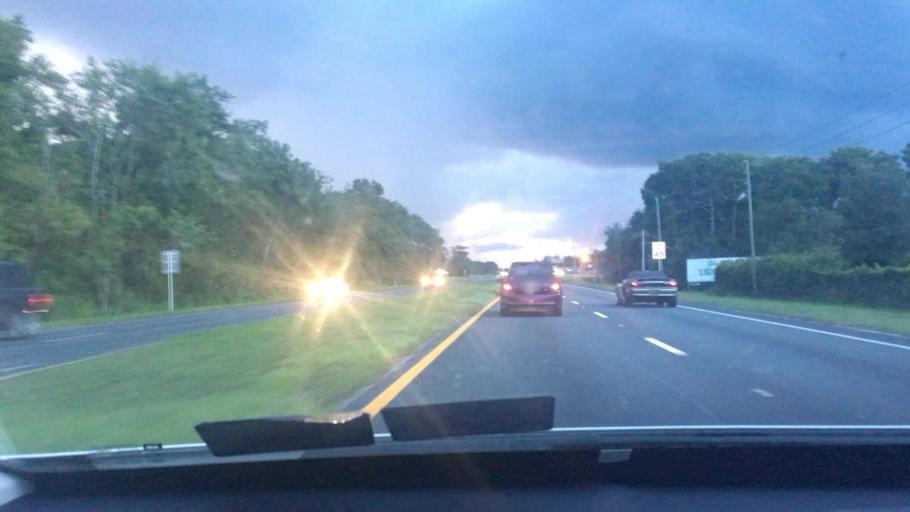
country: US
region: Florida
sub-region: Orange County
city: Bithlo
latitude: 28.5542
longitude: -81.1081
